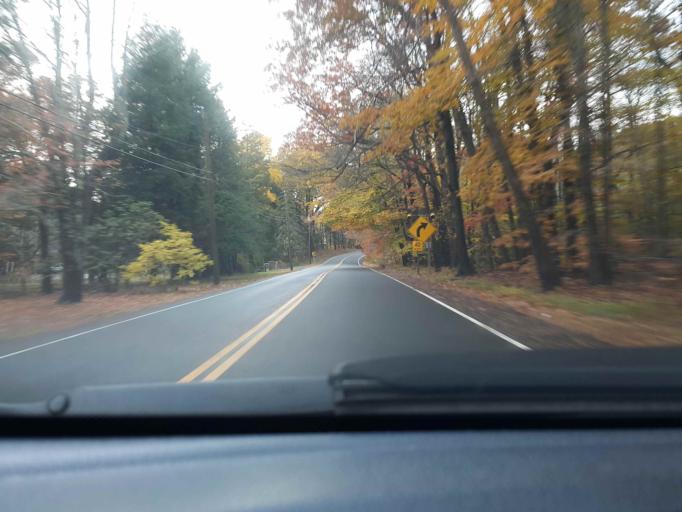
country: US
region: Connecticut
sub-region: New Haven County
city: North Branford
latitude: 41.3408
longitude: -72.7135
